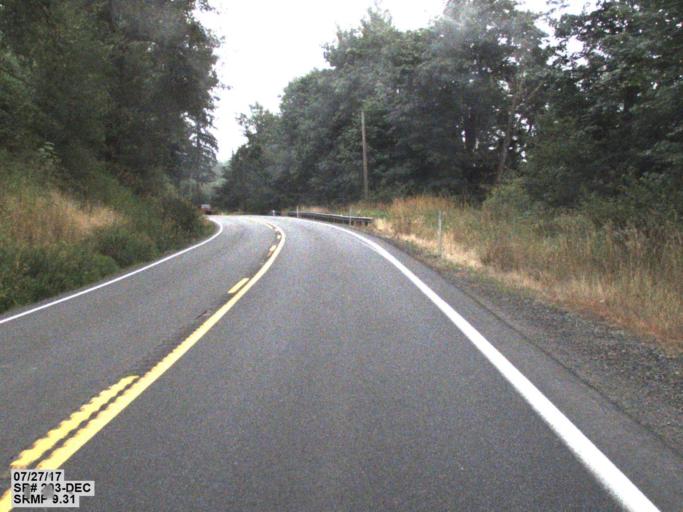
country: US
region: Washington
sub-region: King County
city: Lake Marcel-Stillwater
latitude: 47.6852
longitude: -121.9301
